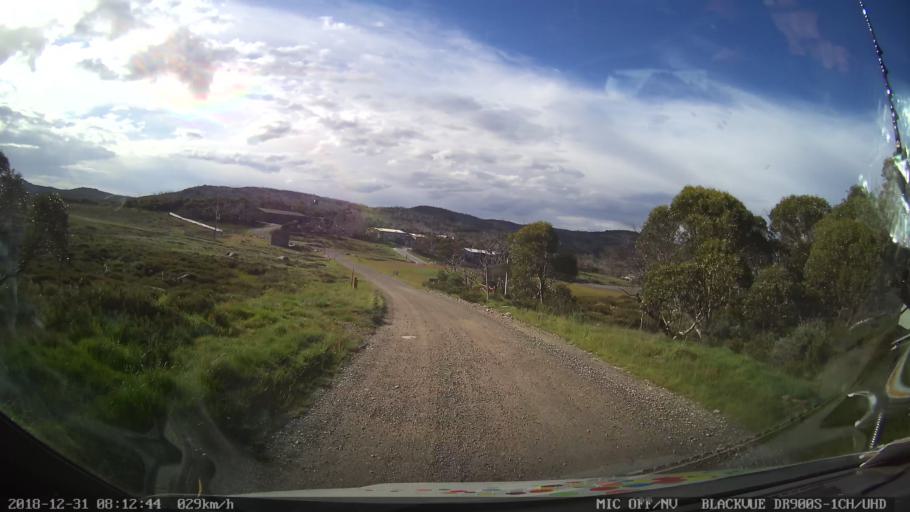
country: AU
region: New South Wales
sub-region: Snowy River
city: Jindabyne
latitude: -36.3889
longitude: 148.4290
